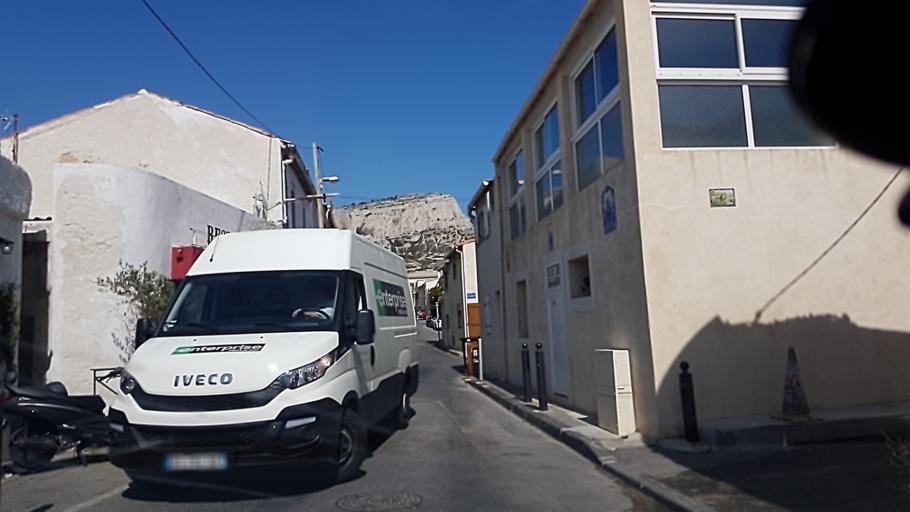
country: FR
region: Provence-Alpes-Cote d'Azur
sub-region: Departement des Bouches-du-Rhone
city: Marseille 08
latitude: 43.2151
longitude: 5.3459
